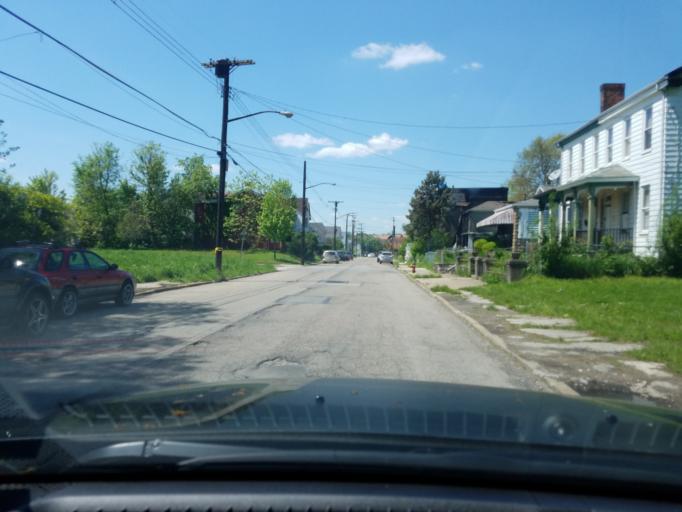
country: US
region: Pennsylvania
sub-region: Allegheny County
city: Aspinwall
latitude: 40.4640
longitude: -79.9130
